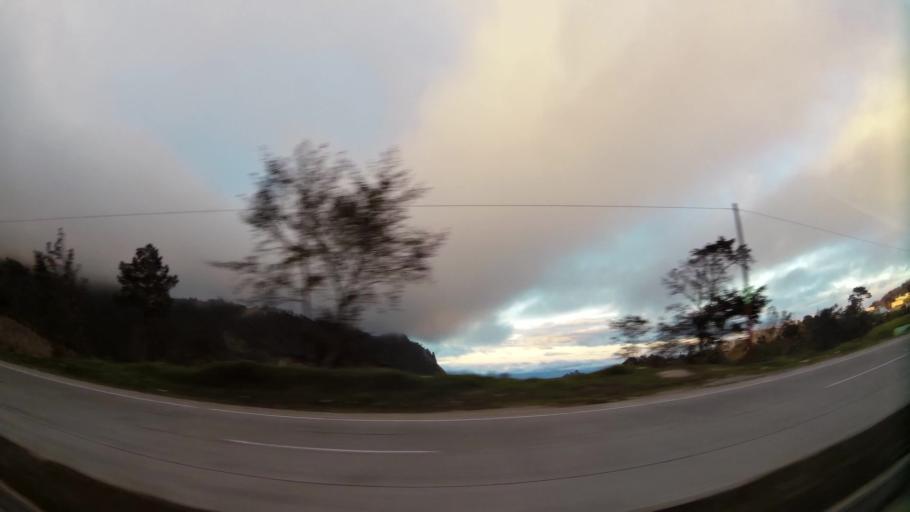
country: GT
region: Solola
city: Concepcion
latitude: 14.8387
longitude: -91.1346
